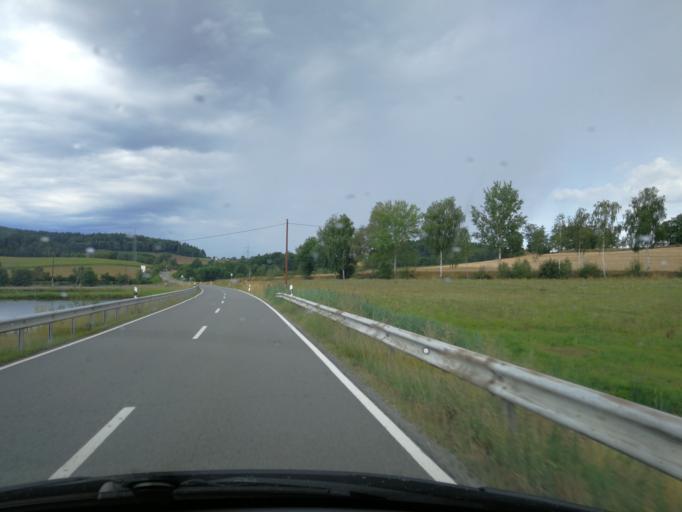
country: DE
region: Bavaria
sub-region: Upper Palatinate
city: Brennberg
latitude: 49.0766
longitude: 12.3871
